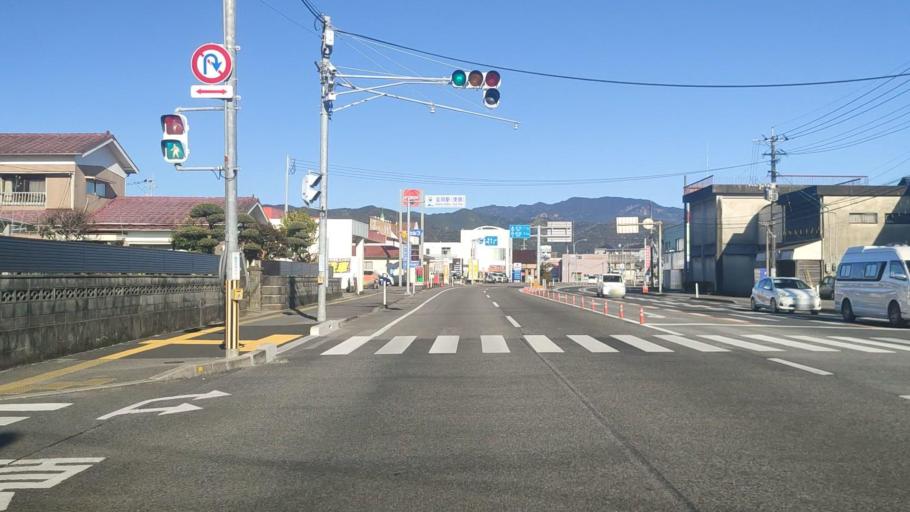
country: JP
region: Miyazaki
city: Nobeoka
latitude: 32.5903
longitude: 131.6758
